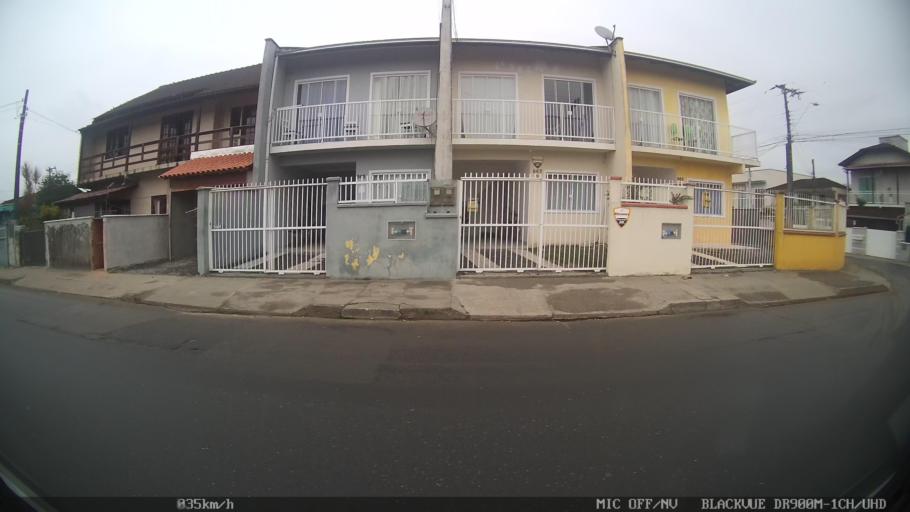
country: BR
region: Santa Catarina
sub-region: Joinville
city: Joinville
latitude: -26.2416
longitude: -48.8100
